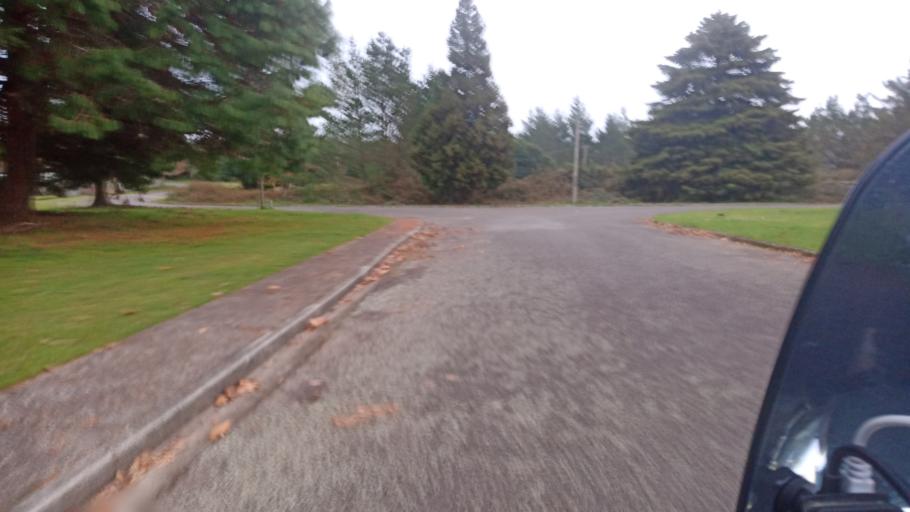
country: NZ
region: Bay of Plenty
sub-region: Whakatane District
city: Murupara
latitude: -38.6394
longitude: 176.7324
